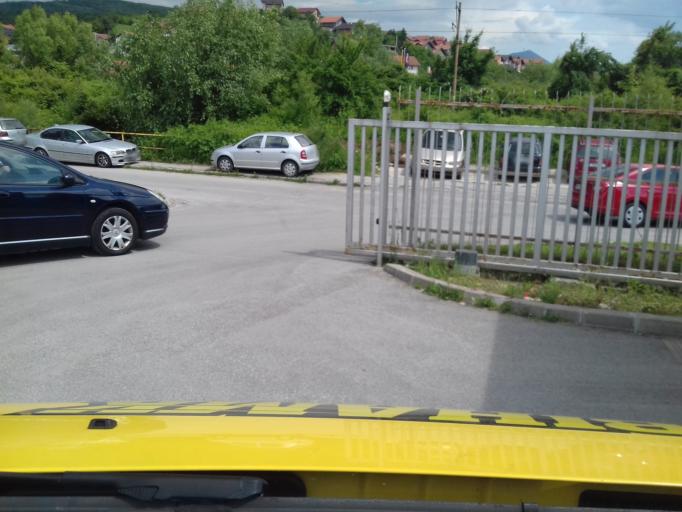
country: BA
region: Federation of Bosnia and Herzegovina
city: Vogosca
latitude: 43.8791
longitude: 18.3133
